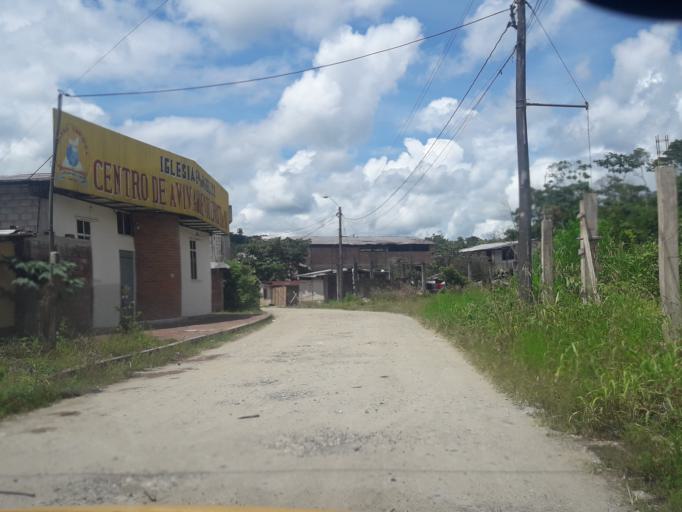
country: EC
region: Napo
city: Tena
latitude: -1.0069
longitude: -77.8190
